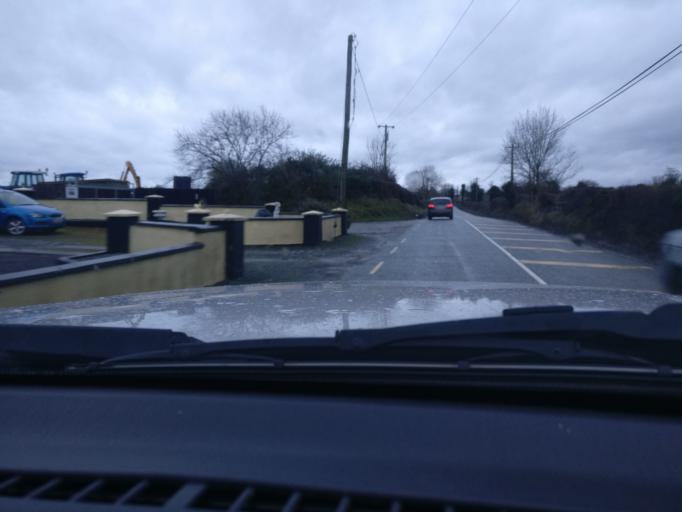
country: IE
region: Leinster
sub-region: An Mhi
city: Longwood
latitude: 53.4630
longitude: -6.9159
